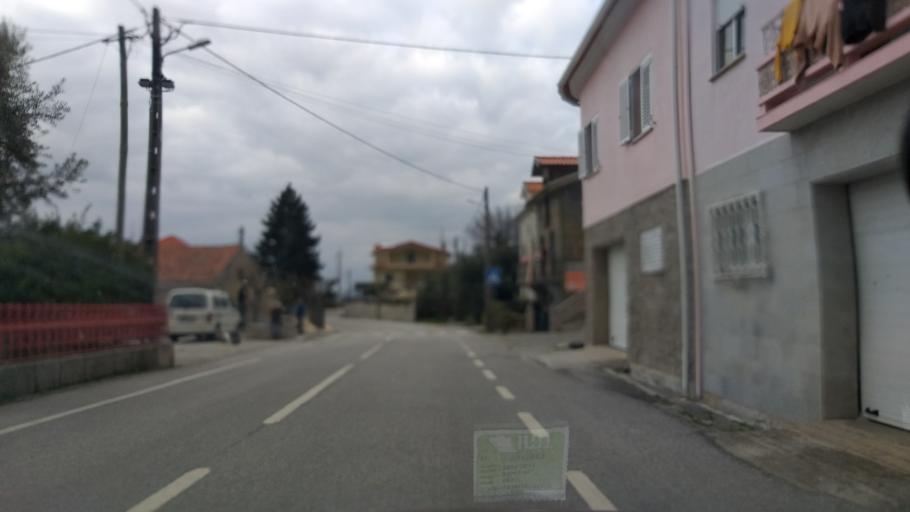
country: PT
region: Guarda
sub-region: Seia
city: Seia
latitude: 40.4769
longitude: -7.6327
